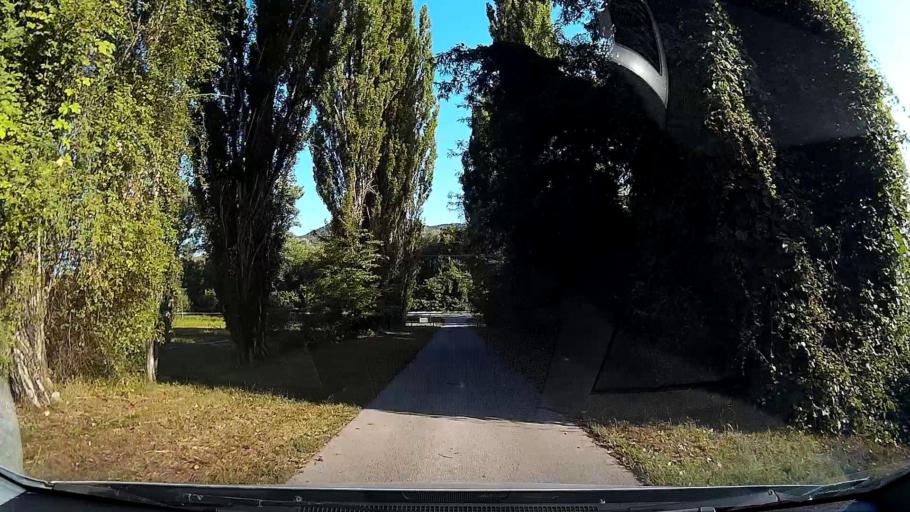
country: HU
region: Pest
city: Nagymaros
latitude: 47.7607
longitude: 18.9383
